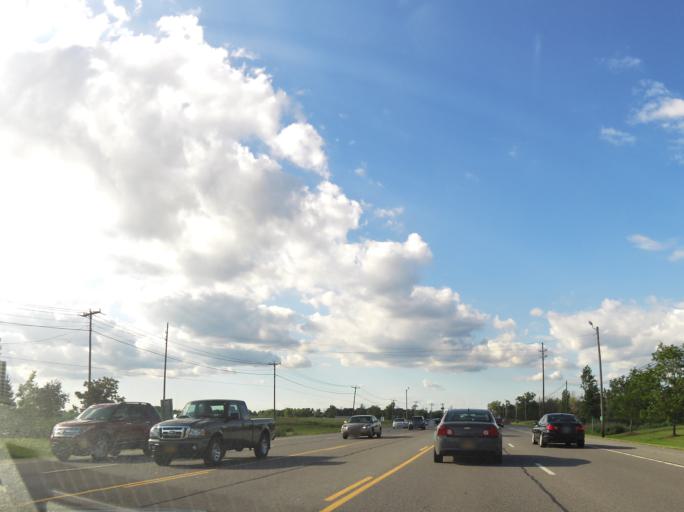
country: US
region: New York
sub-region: Erie County
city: Harris Hill
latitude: 42.9407
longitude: -78.6970
